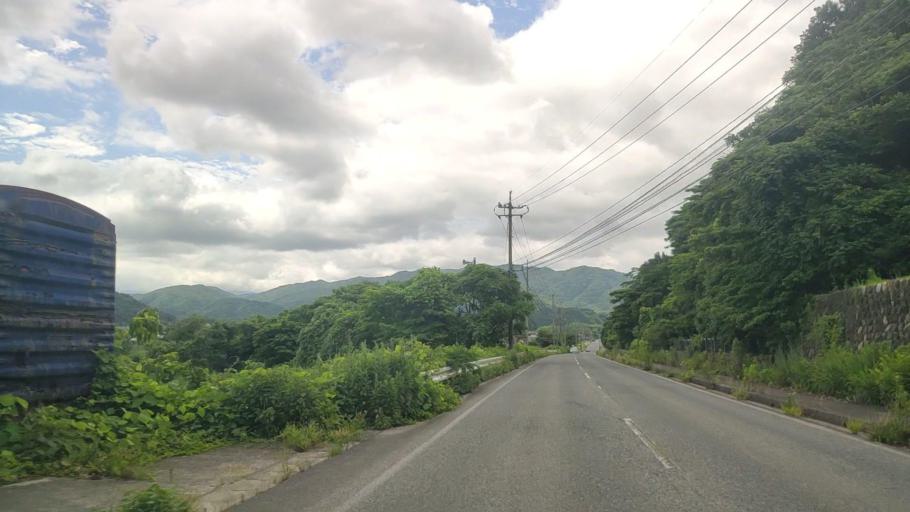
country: JP
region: Tottori
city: Yonago
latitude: 35.3374
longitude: 133.4342
